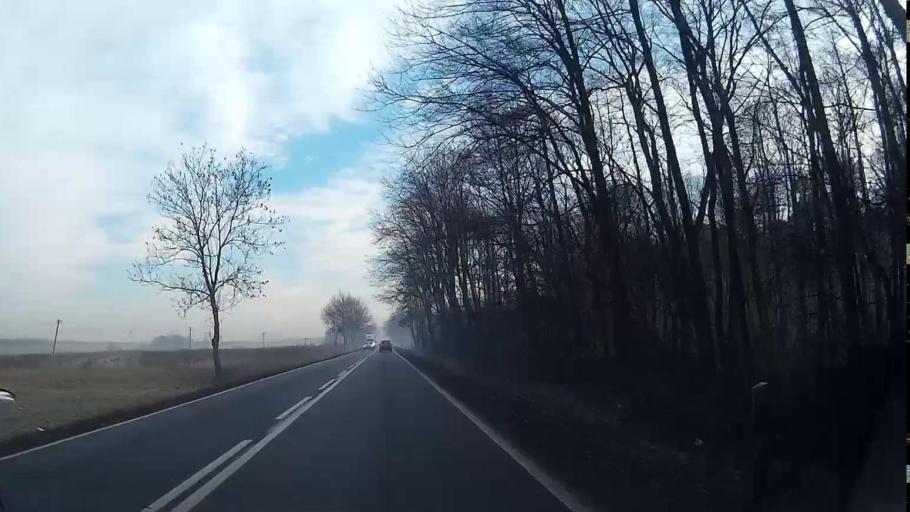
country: PL
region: Lesser Poland Voivodeship
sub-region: Powiat krakowski
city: Sanka
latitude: 50.0346
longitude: 19.6472
